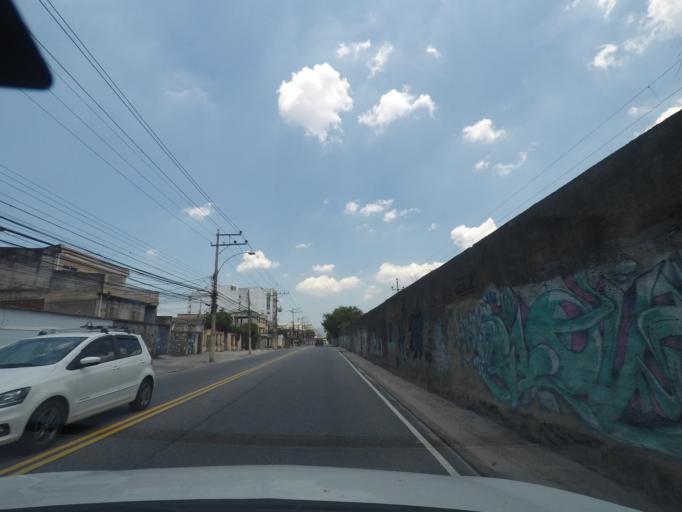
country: BR
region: Rio de Janeiro
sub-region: Sao Joao De Meriti
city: Sao Joao de Meriti
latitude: -22.8714
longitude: -43.3462
